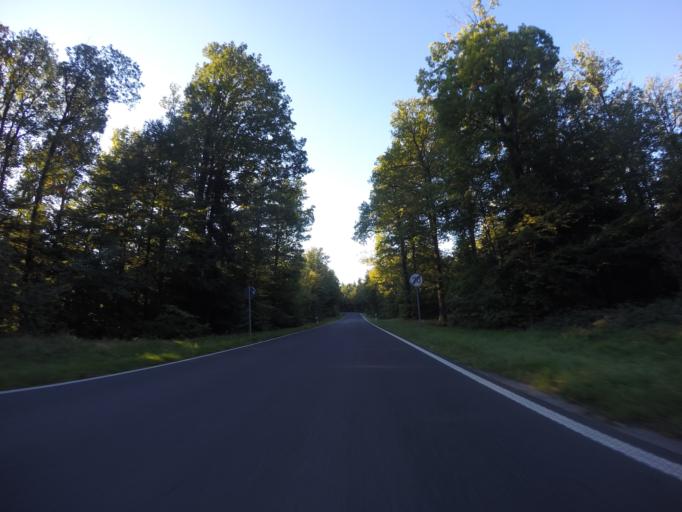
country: DE
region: Bavaria
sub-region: Regierungsbezirk Unterfranken
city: Altenbuch
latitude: 49.8830
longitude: 9.4013
